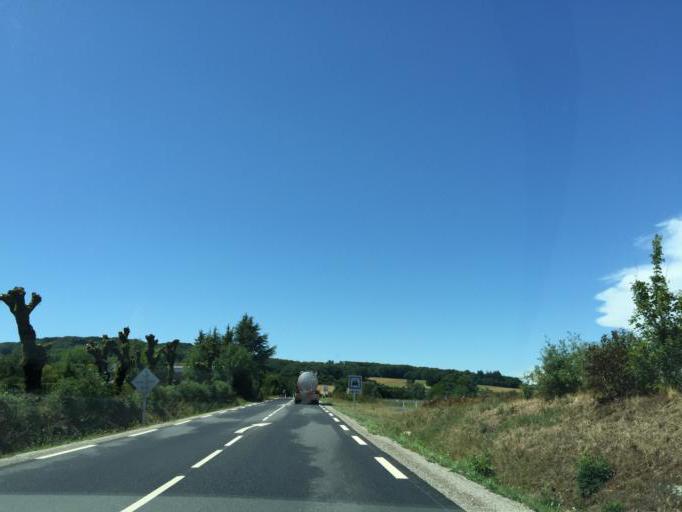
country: FR
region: Midi-Pyrenees
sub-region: Departement de l'Aveyron
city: Salles-Curan
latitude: 44.2403
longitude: 2.9165
